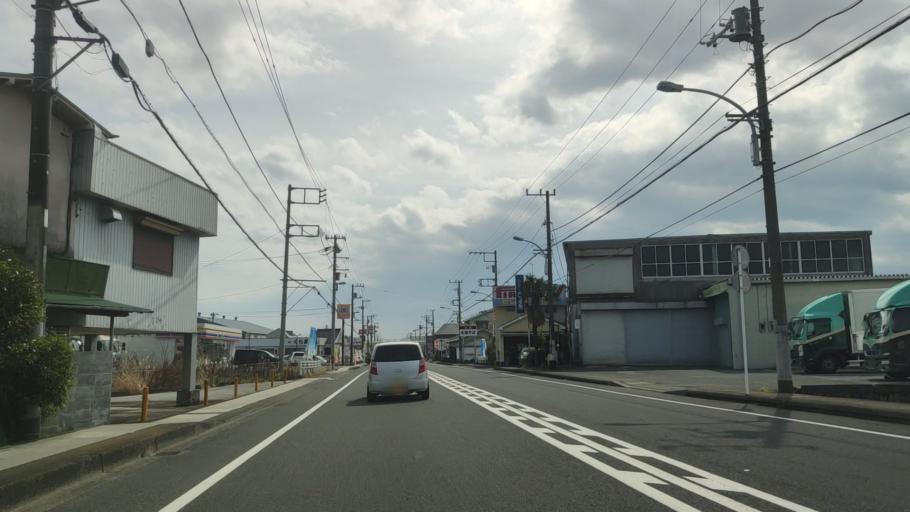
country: JP
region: Kanagawa
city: Odawara
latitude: 35.3159
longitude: 139.1606
